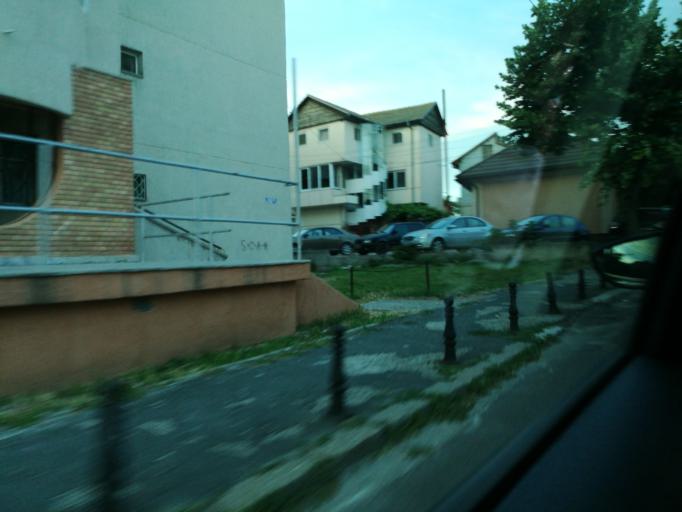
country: RO
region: Constanta
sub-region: Municipiul Mangalia
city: Mangalia
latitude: 43.8146
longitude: 28.5826
